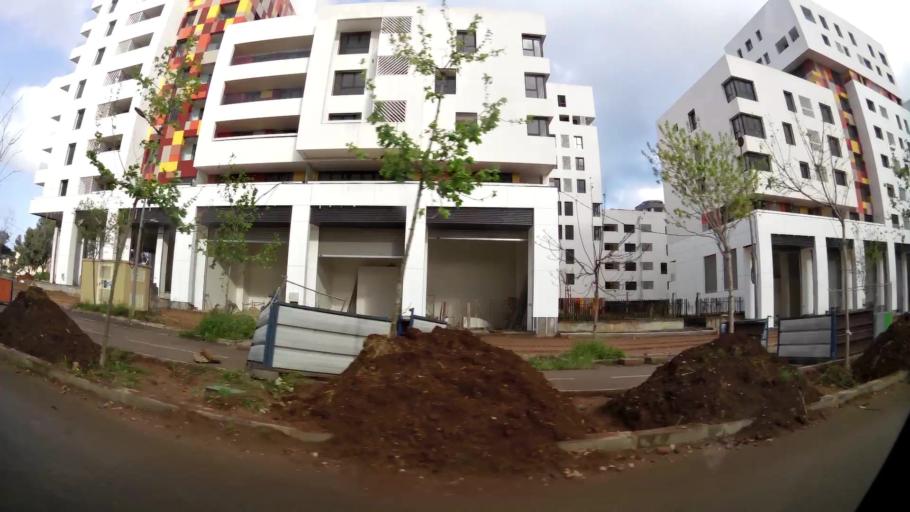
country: MA
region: Grand Casablanca
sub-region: Casablanca
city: Casablanca
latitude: 33.5581
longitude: -7.6521
